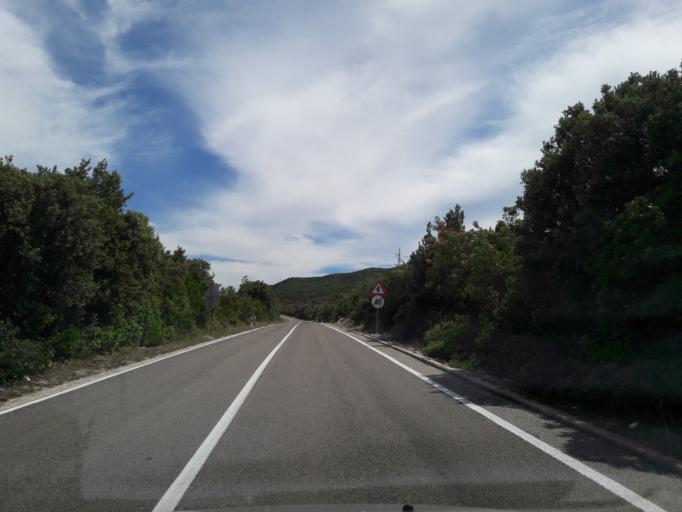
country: HR
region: Dubrovacko-Neretvanska
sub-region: Grad Dubrovnik
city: Opuzen
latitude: 42.9091
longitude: 17.4769
